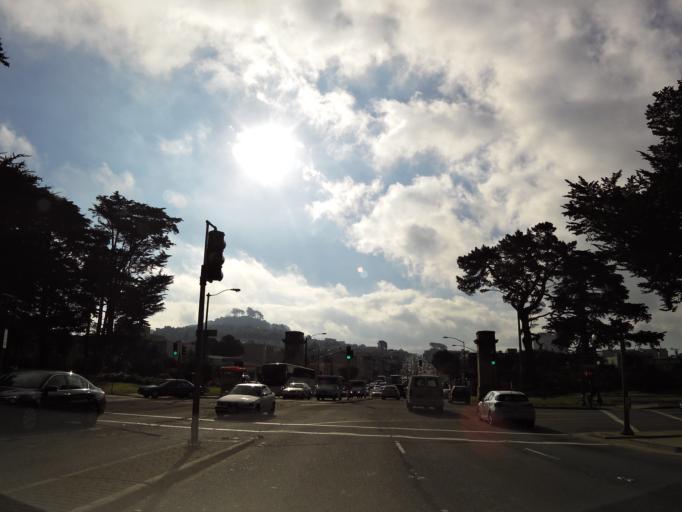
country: US
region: California
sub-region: San Francisco County
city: San Francisco
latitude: 37.7664
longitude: -122.4776
